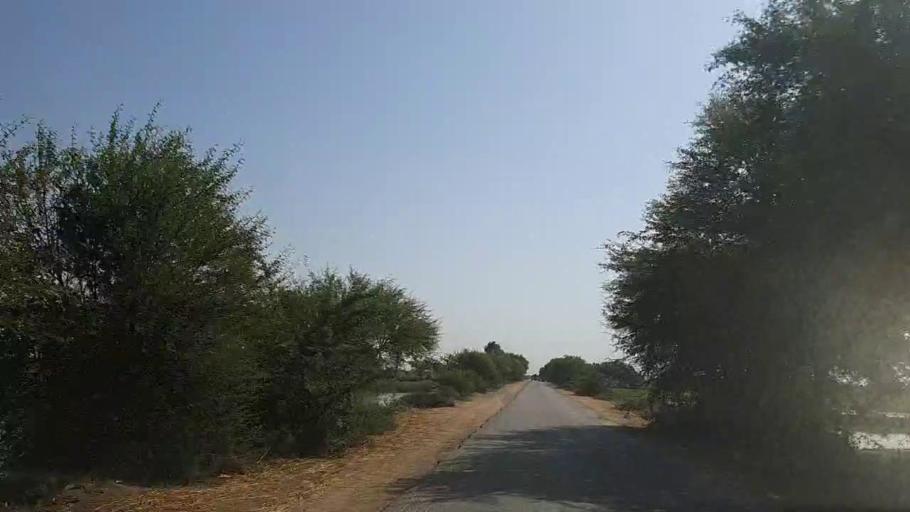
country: PK
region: Sindh
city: Mirpur Batoro
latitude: 24.6561
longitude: 68.2872
